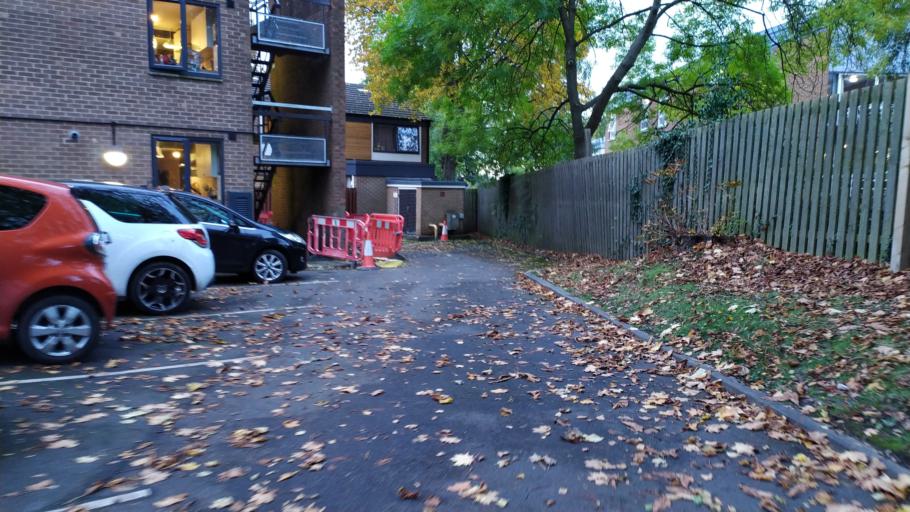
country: GB
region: England
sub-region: City and Borough of Leeds
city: Leeds
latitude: 53.8203
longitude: -1.5701
